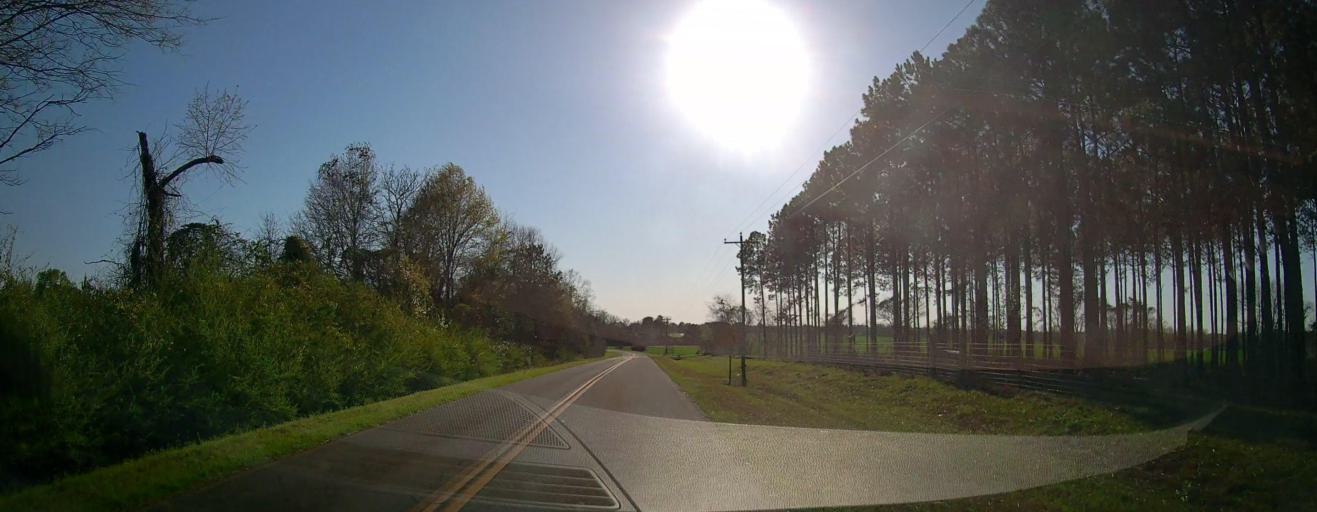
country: US
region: Georgia
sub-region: Pulaski County
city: Hawkinsville
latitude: 32.3244
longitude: -83.5664
